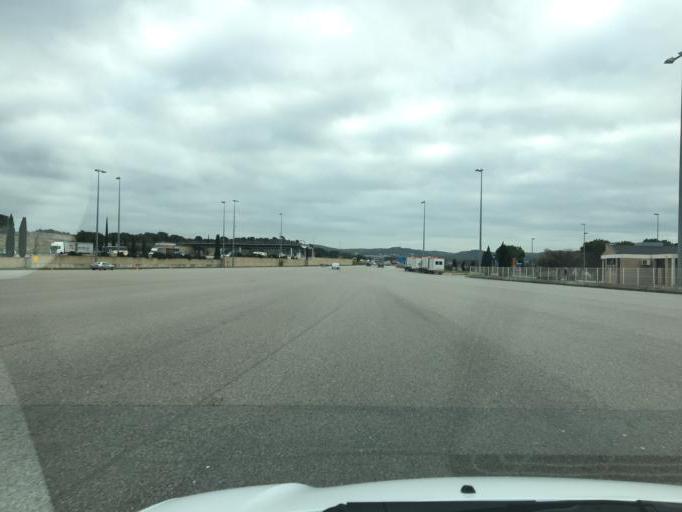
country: FR
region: Provence-Alpes-Cote d'Azur
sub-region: Departement des Bouches-du-Rhone
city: Lancon-Provence
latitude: 43.5933
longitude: 5.1731
